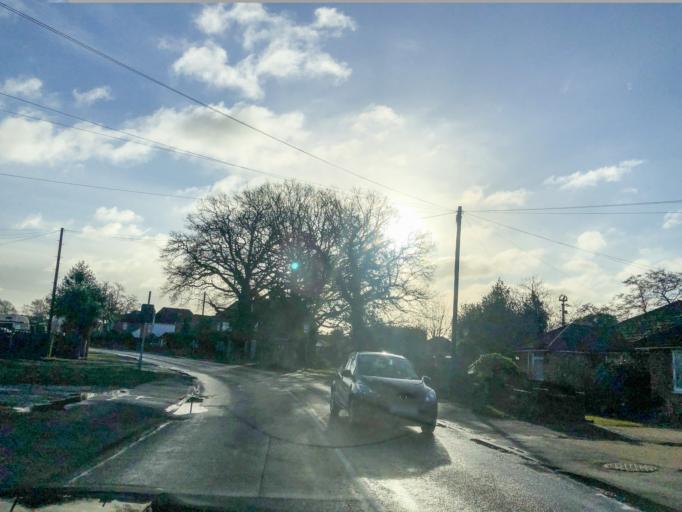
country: GB
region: England
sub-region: Hampshire
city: Farnborough
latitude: 51.2930
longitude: -0.7361
